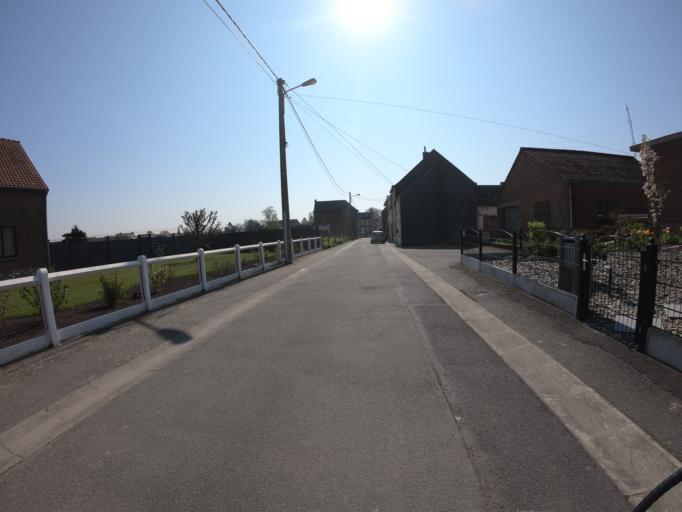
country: BE
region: Wallonia
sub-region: Province du Hainaut
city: Lessines
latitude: 50.7337
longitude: 3.8463
